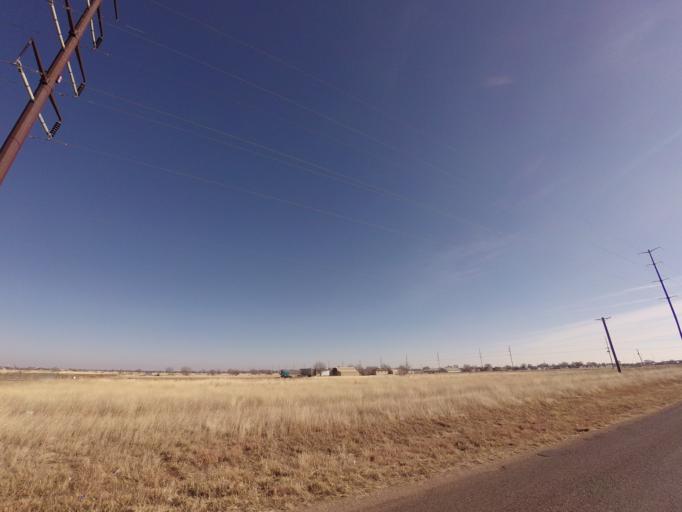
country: US
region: New Mexico
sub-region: Curry County
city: Clovis
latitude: 34.4135
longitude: -103.2493
